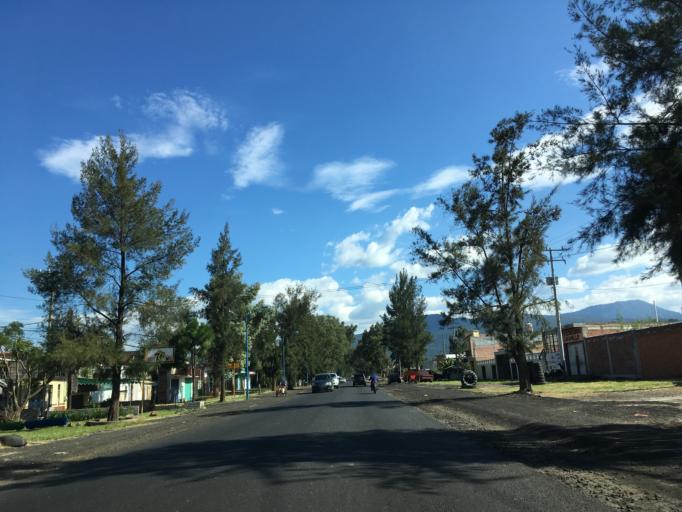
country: MX
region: Michoacan
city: Zacapu
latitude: 19.7973
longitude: -101.7758
